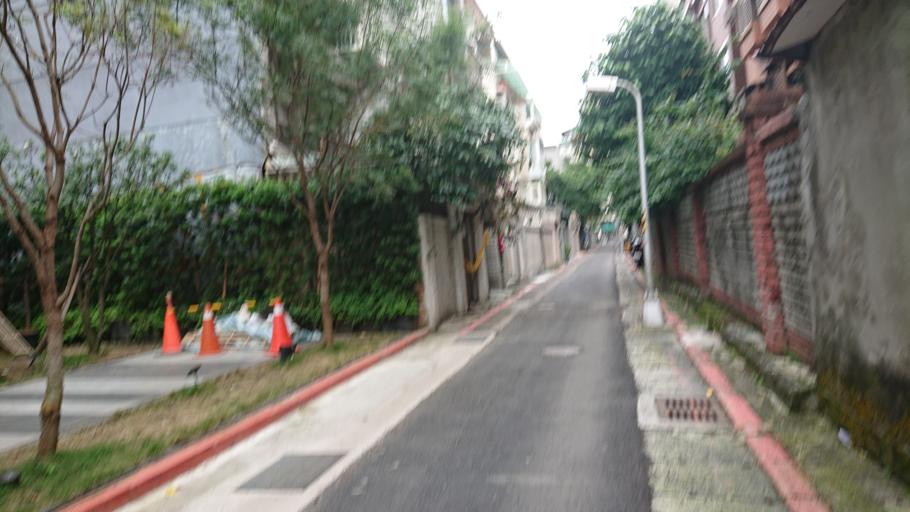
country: TW
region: Taipei
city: Taipei
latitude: 25.0398
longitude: 121.5337
